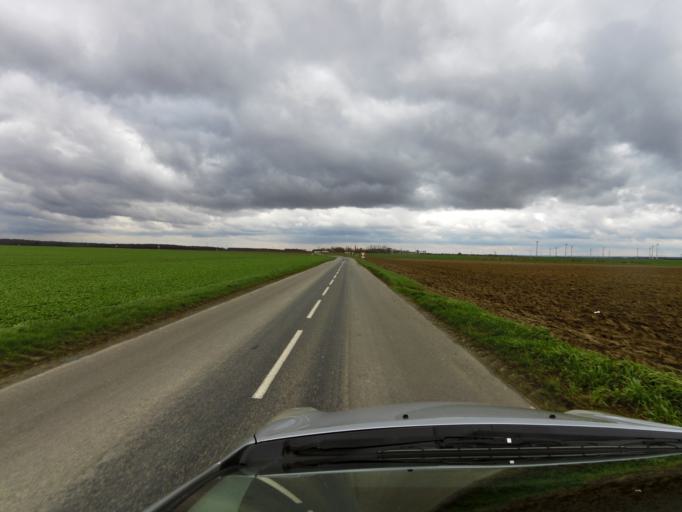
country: FR
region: Picardie
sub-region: Departement de la Somme
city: Roye
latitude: 49.7416
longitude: 2.8064
